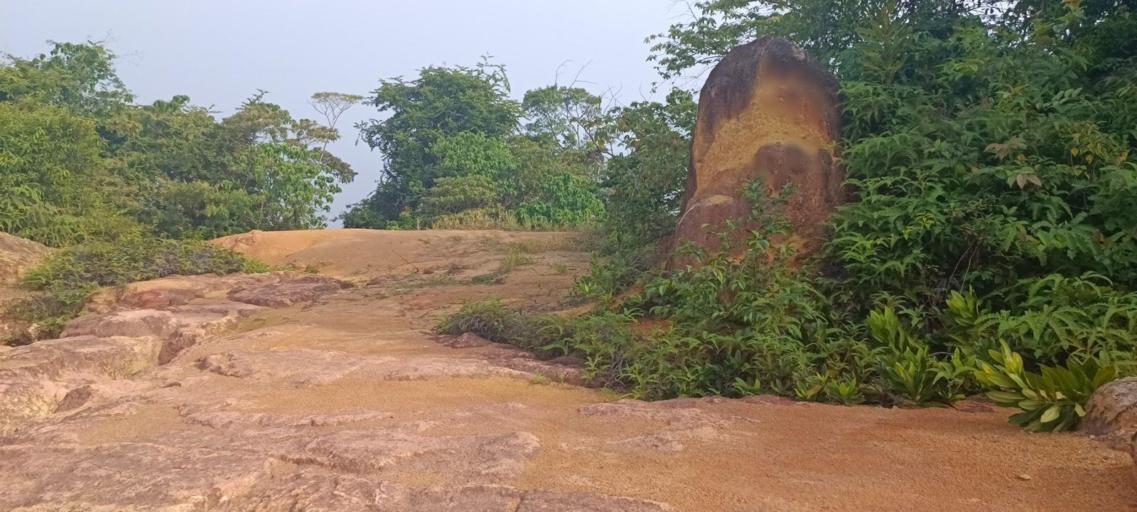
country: MY
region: Penang
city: Juru
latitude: 5.2737
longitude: 100.4196
